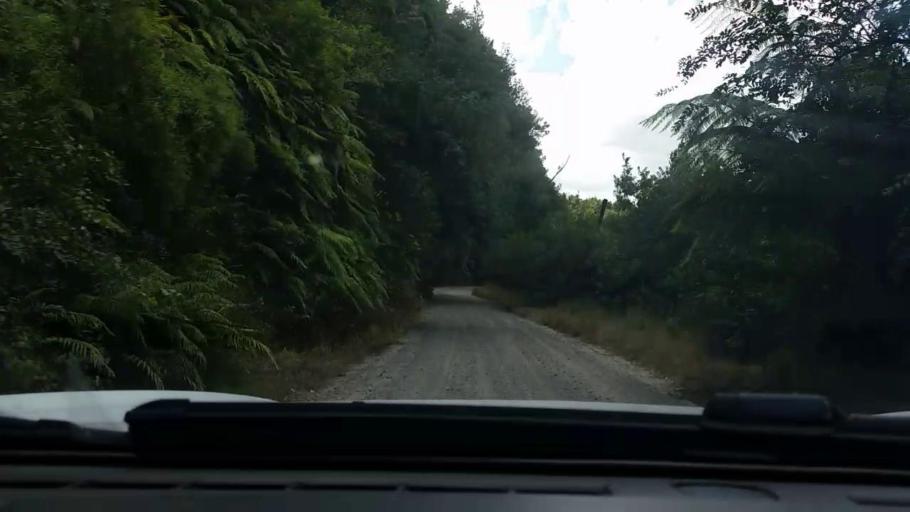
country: NZ
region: Bay of Plenty
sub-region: Kawerau District
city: Kawerau
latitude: -38.0278
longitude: 176.5590
